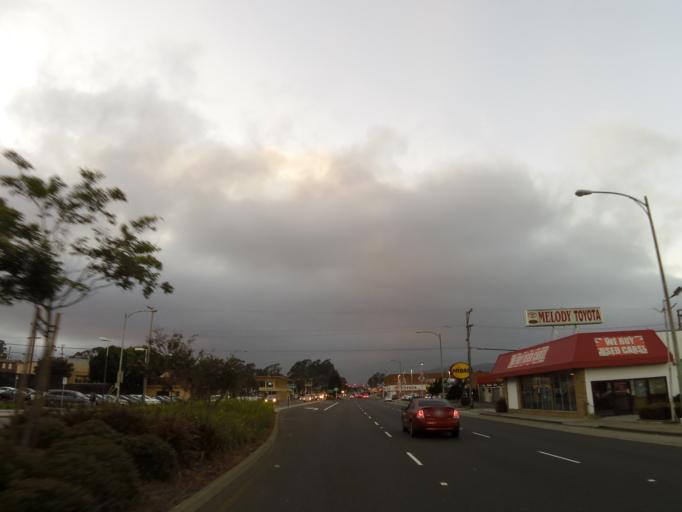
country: US
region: California
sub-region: San Mateo County
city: San Bruno
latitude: 37.6265
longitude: -122.4150
